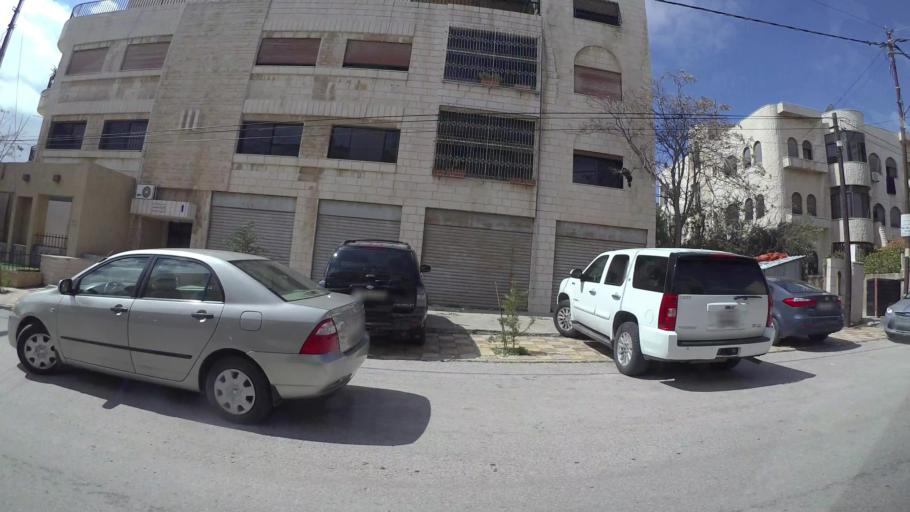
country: JO
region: Amman
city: Wadi as Sir
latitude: 31.9554
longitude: 35.8394
